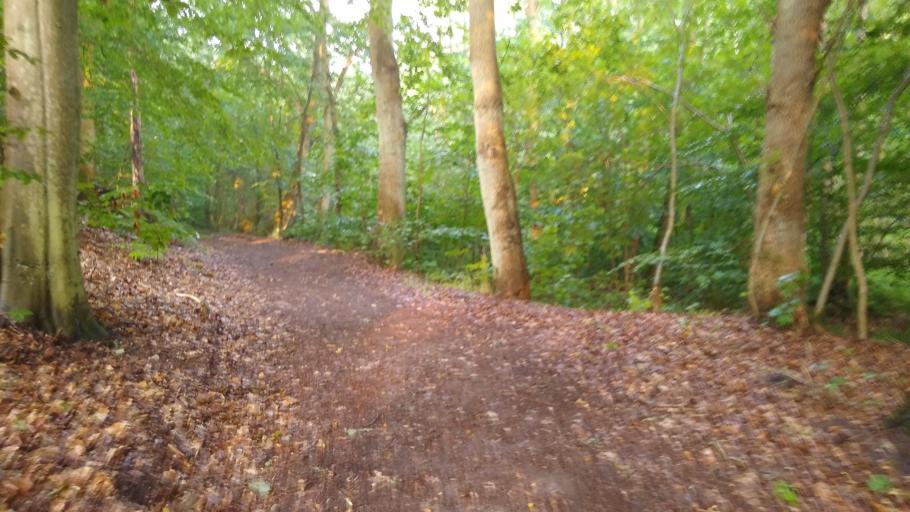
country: DK
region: South Denmark
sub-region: Fredericia Kommune
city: Fredericia
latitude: 55.6055
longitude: 9.7110
